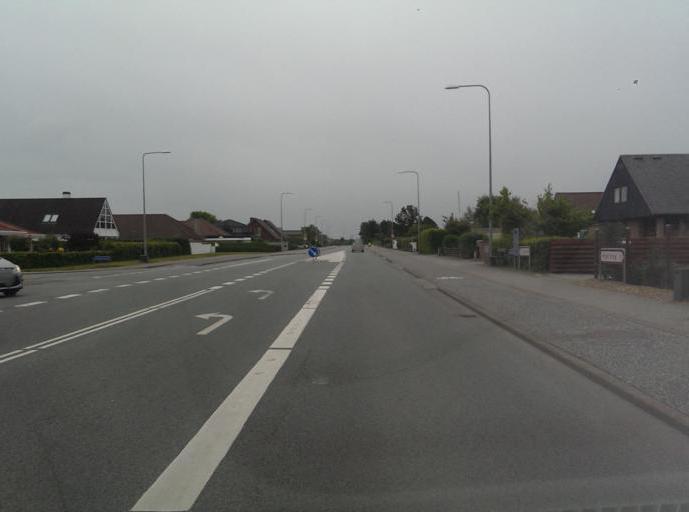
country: DK
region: South Denmark
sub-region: Fano Kommune
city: Nordby
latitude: 55.5035
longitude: 8.3868
